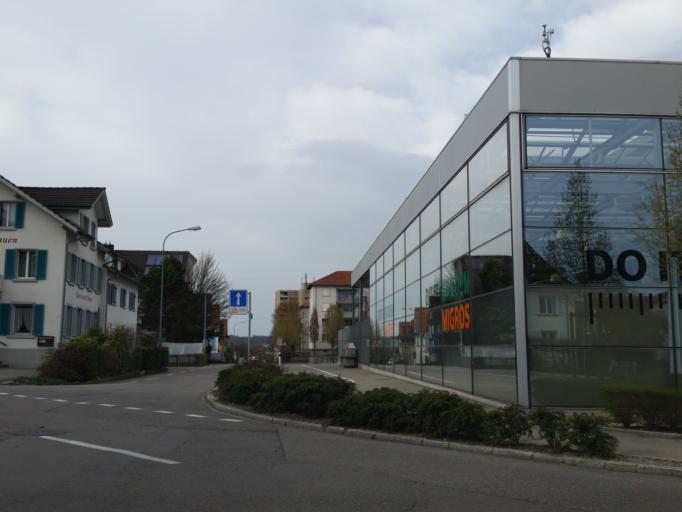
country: CH
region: Thurgau
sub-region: Arbon District
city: Amriswil
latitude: 47.5476
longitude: 9.2964
